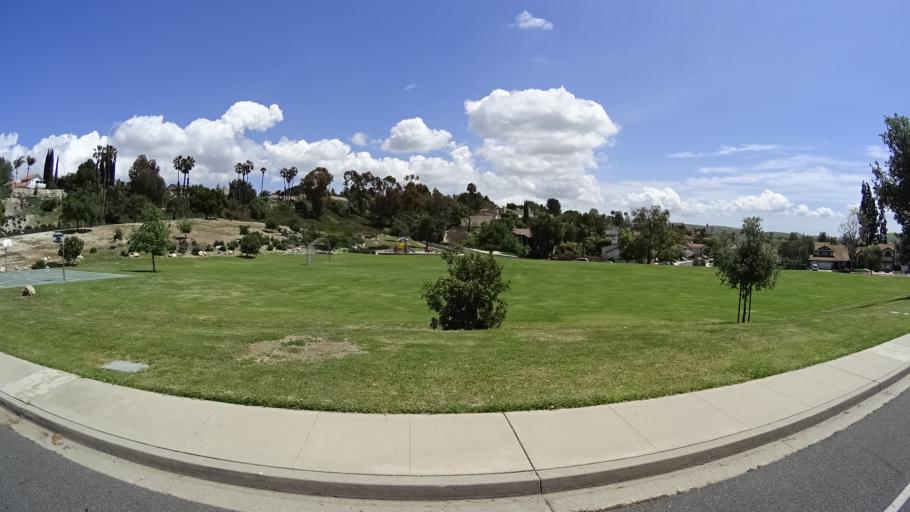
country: US
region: California
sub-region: Ventura County
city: Thousand Oaks
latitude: 34.2251
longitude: -118.8430
